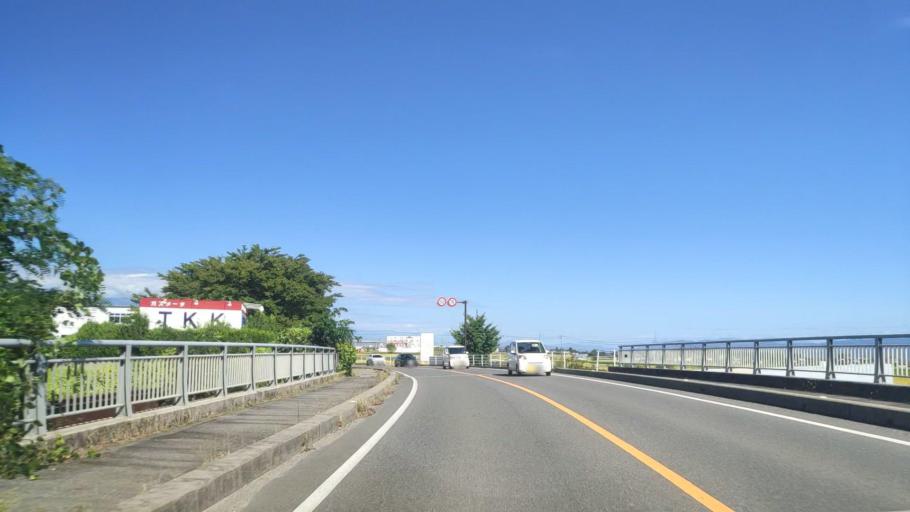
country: JP
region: Nagano
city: Matsumoto
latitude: 36.1846
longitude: 137.9049
